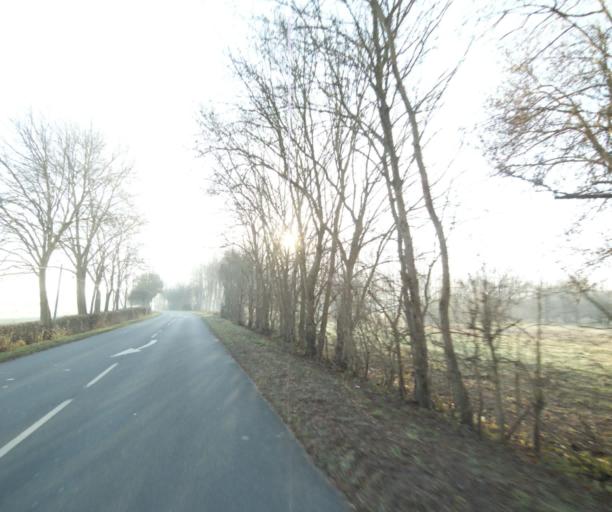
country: FR
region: Poitou-Charentes
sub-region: Departement de la Charente-Maritime
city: Cherac
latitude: 45.6876
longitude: -0.4619
